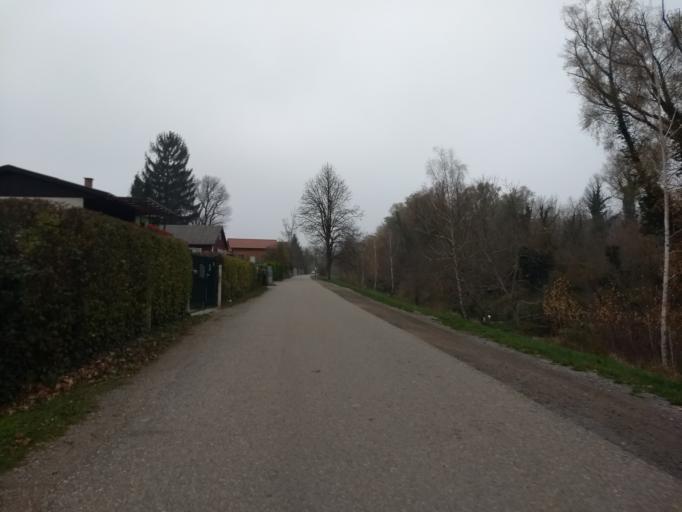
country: AT
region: Lower Austria
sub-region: Politischer Bezirk Tulln
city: Wordern
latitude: 48.3447
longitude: 16.2206
